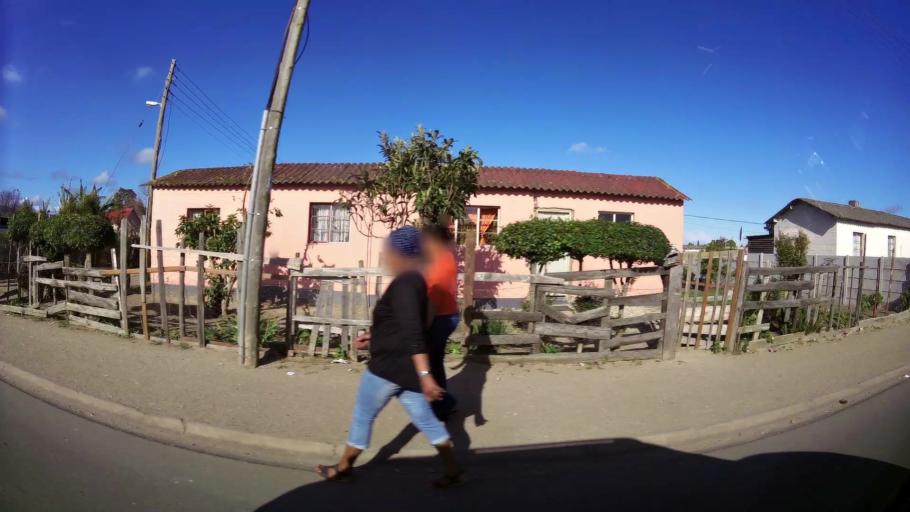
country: ZA
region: Western Cape
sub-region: Eden District Municipality
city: George
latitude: -33.9715
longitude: 22.4795
